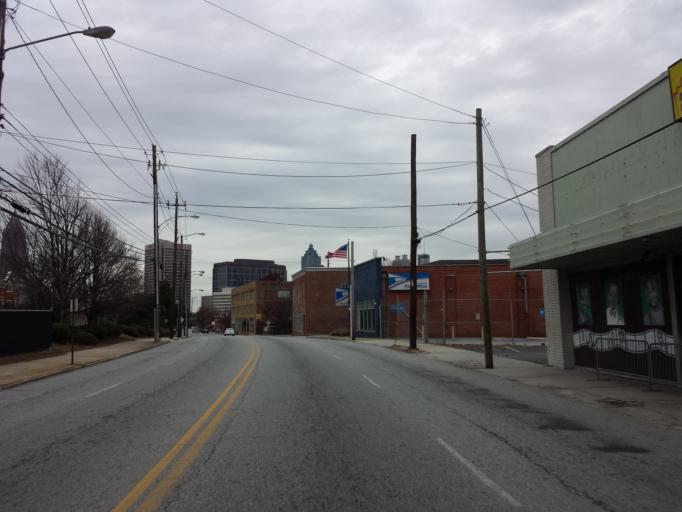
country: US
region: Georgia
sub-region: Fulton County
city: Atlanta
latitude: 33.7741
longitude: -84.4057
